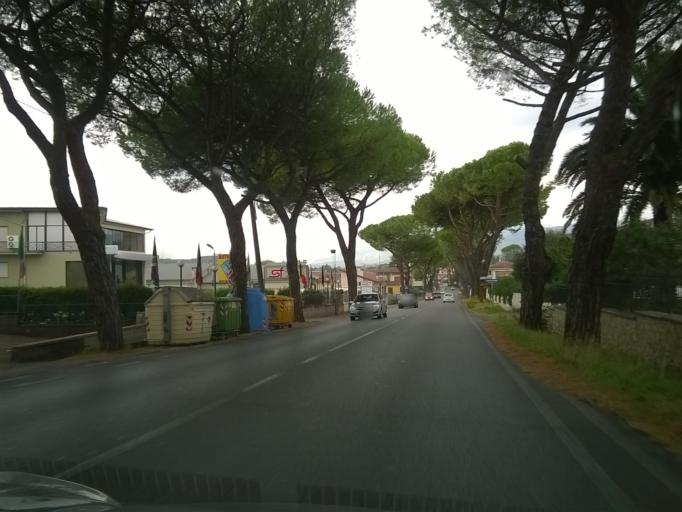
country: IT
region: Tuscany
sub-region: Provincia di Pistoia
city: Borgo a Buggiano
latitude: 43.8785
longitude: 10.7243
